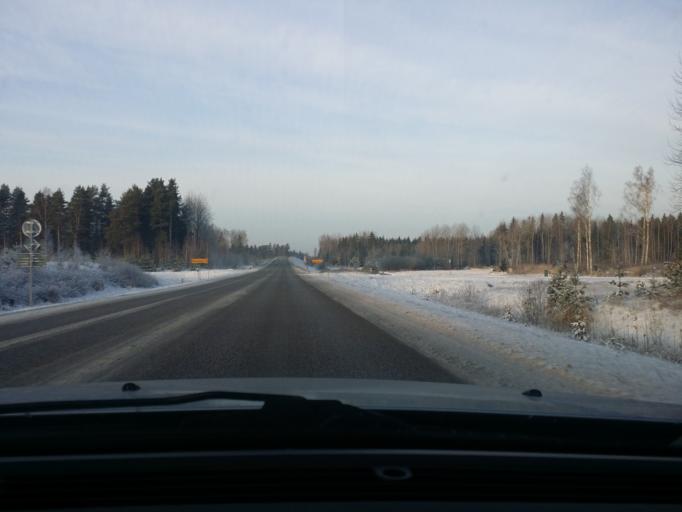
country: SE
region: OErebro
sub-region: Lindesbergs Kommun
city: Frovi
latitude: 59.4667
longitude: 15.4150
